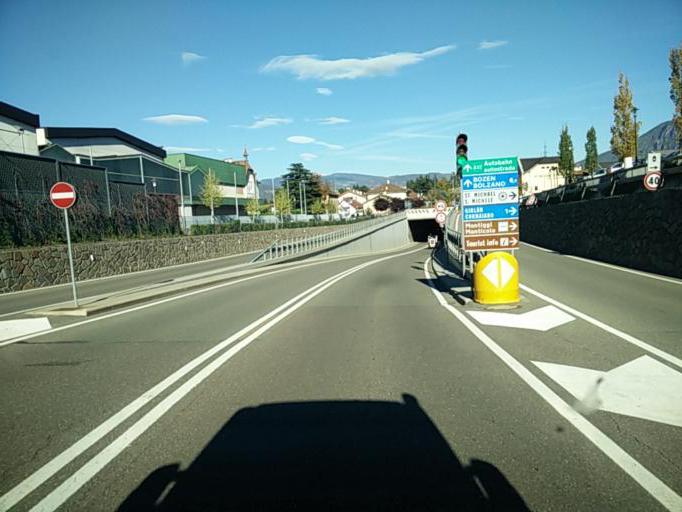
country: IT
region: Trentino-Alto Adige
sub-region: Bolzano
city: San Michele
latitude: 46.4517
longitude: 11.2665
